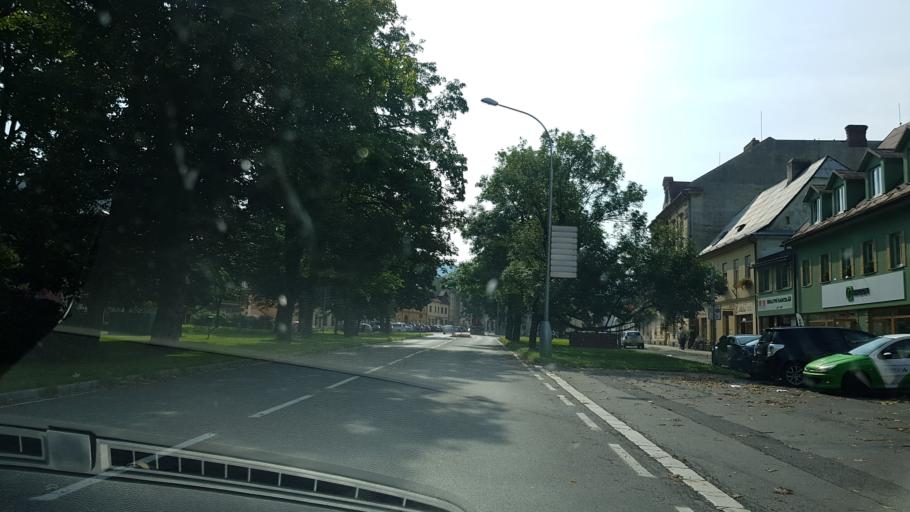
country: CZ
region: Olomoucky
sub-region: Okres Jesenik
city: Jesenik
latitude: 50.2275
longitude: 17.2045
